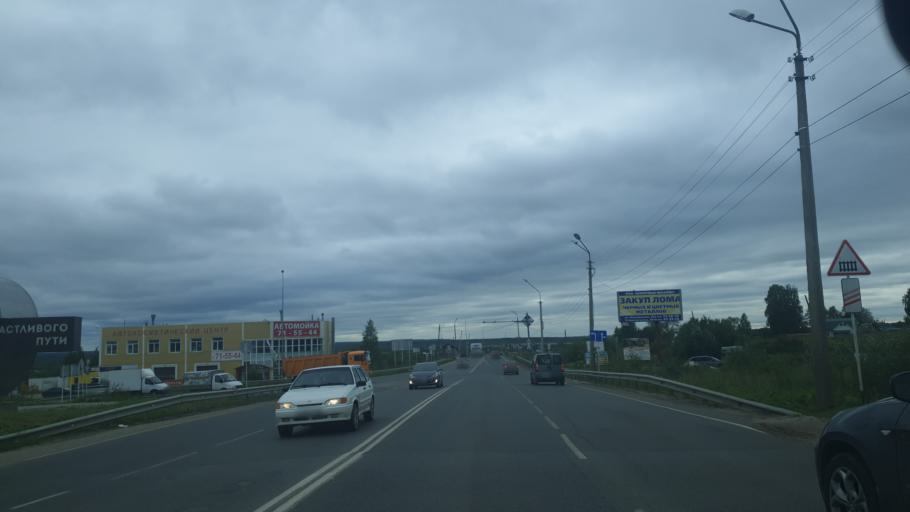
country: RU
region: Komi Republic
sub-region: Syktyvdinskiy Rayon
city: Syktyvkar
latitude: 61.6360
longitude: 50.8121
